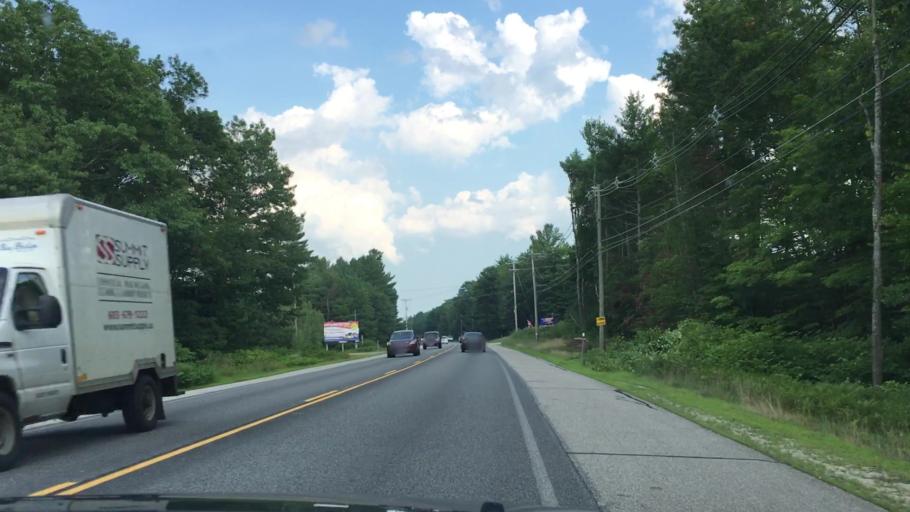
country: US
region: New Hampshire
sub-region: Strafford County
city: Farmington
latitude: 43.3768
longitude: -71.0630
